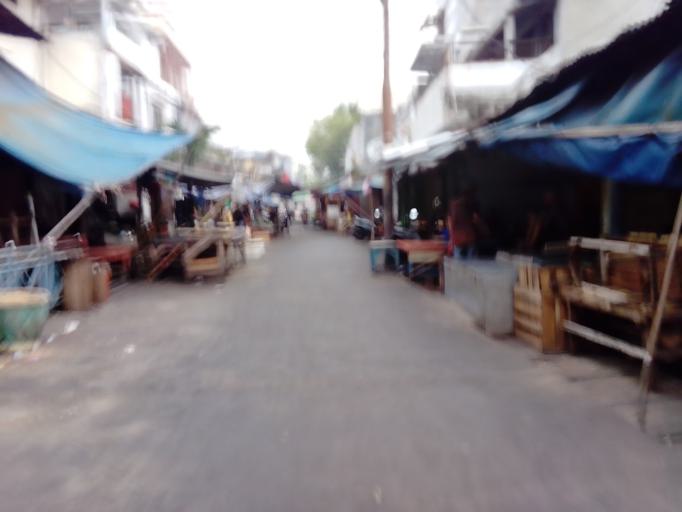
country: ID
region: Jakarta Raya
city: Jakarta
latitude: -6.1433
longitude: 106.8131
